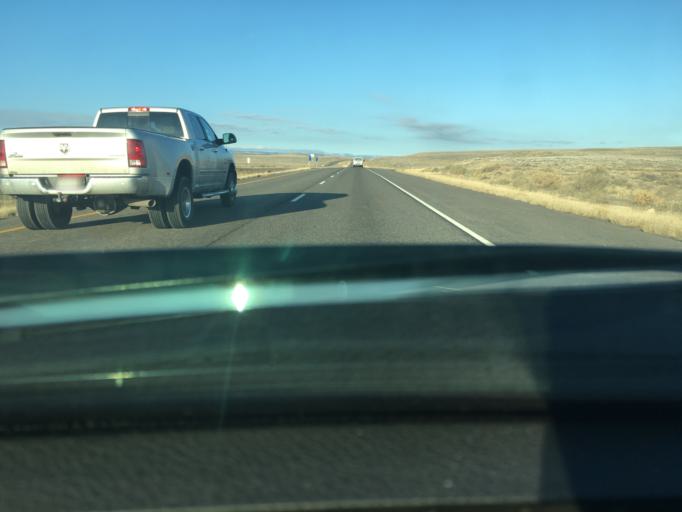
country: US
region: Colorado
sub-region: Delta County
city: Delta
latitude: 38.7659
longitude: -108.2143
